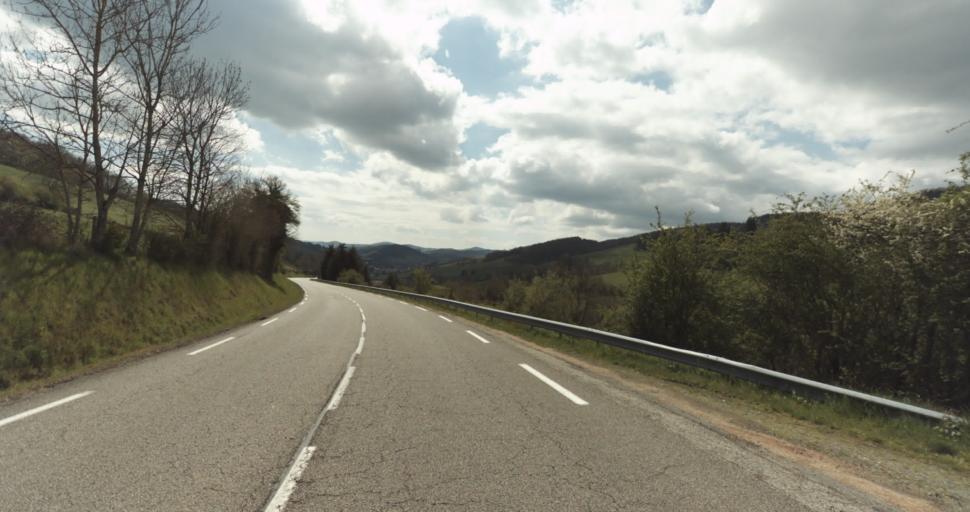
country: FR
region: Rhone-Alpes
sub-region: Departement du Rhone
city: Tarare
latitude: 45.9198
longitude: 4.4131
